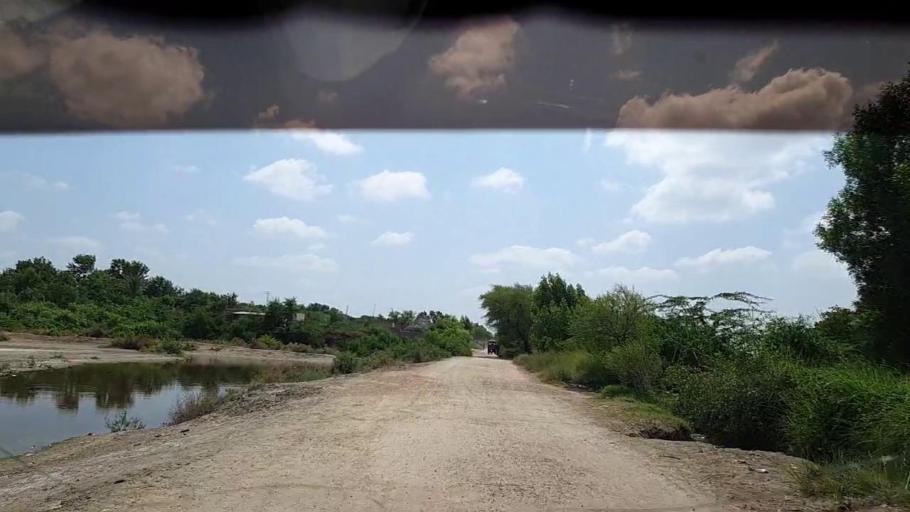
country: PK
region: Sindh
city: Kadhan
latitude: 24.5908
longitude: 68.9579
